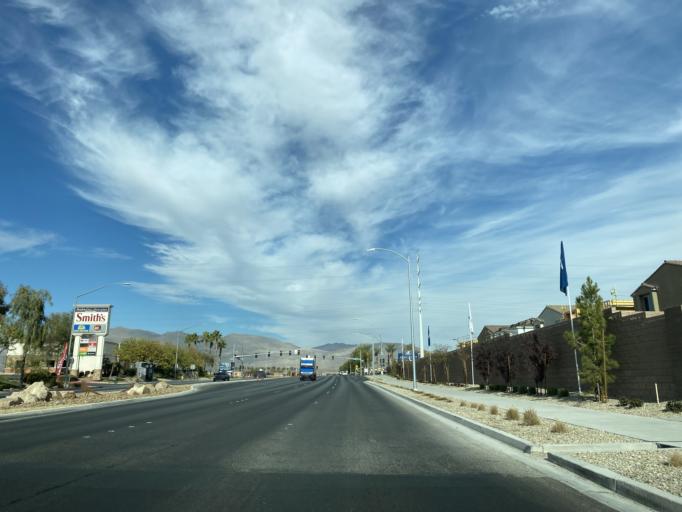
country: US
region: Nevada
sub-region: Clark County
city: Nellis Air Force Base
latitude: 36.2747
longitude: -115.1169
